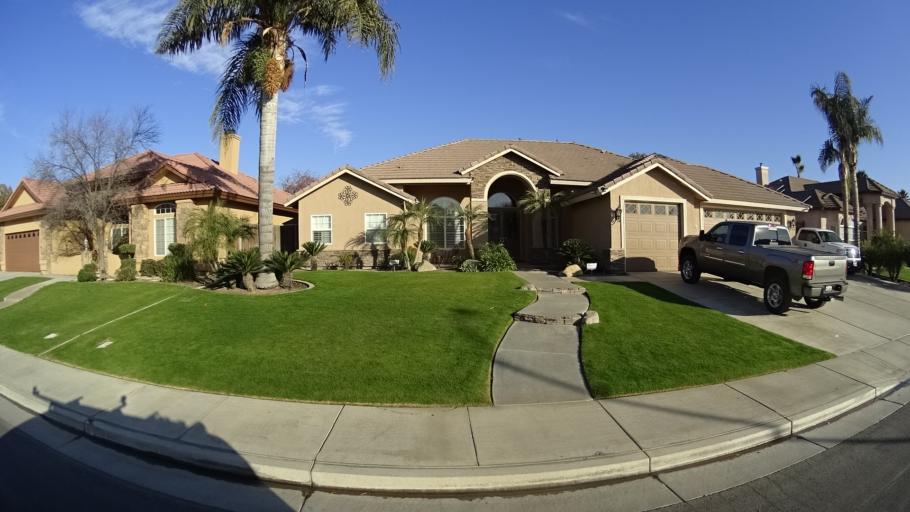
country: US
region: California
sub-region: Kern County
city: Greenfield
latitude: 35.2766
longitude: -119.0524
